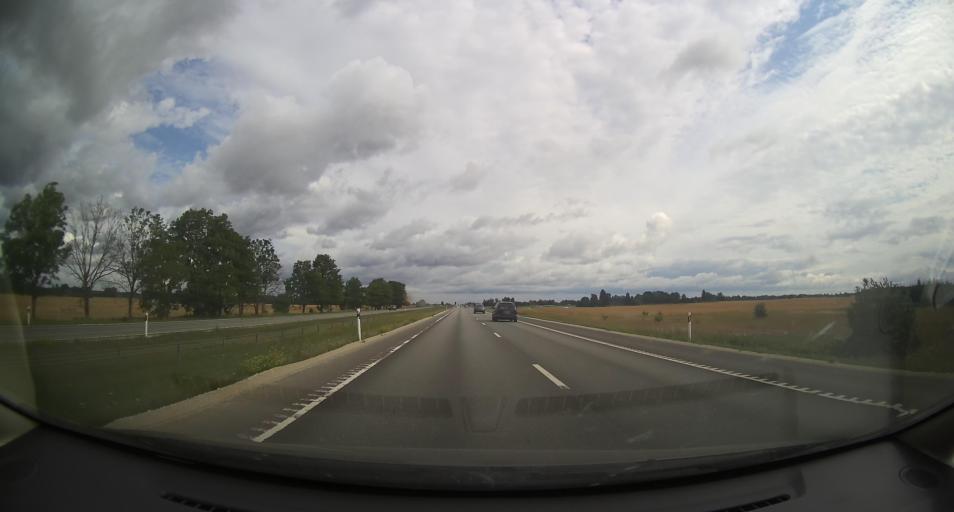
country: EE
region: Harju
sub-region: Saue linn
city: Saue
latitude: 59.2950
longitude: 24.5535
